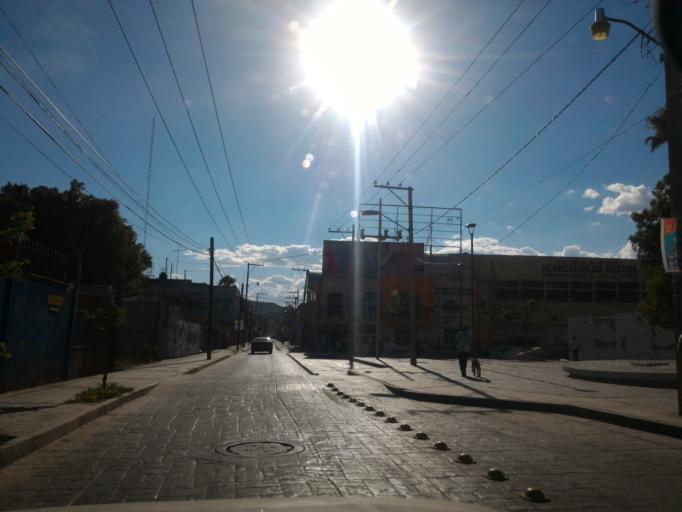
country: MX
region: Guanajuato
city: San Francisco del Rincon
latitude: 21.0291
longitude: -101.8738
